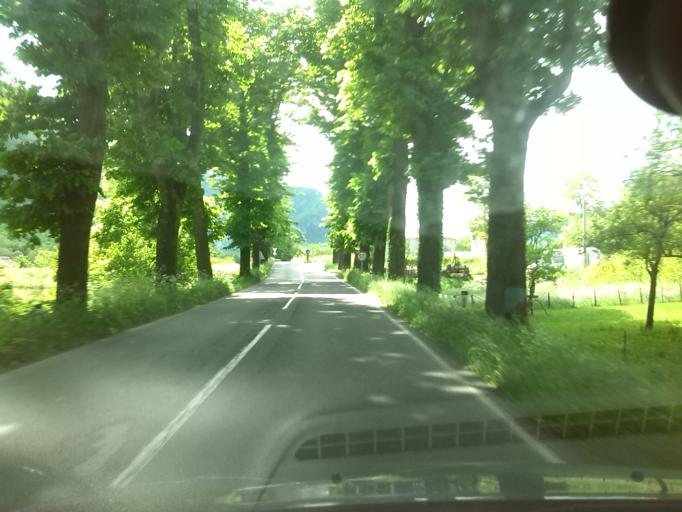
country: SI
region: Kobarid
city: Kobarid
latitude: 46.2458
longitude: 13.5294
